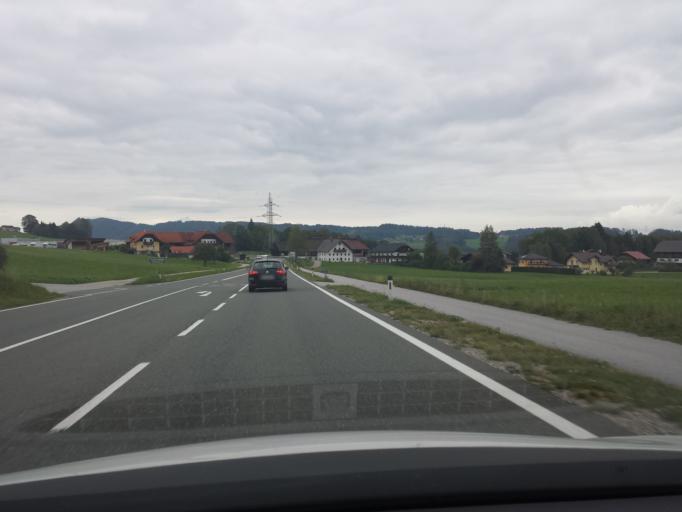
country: AT
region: Salzburg
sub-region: Politischer Bezirk Salzburg-Umgebung
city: Koppl
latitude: 47.8160
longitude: 13.1656
